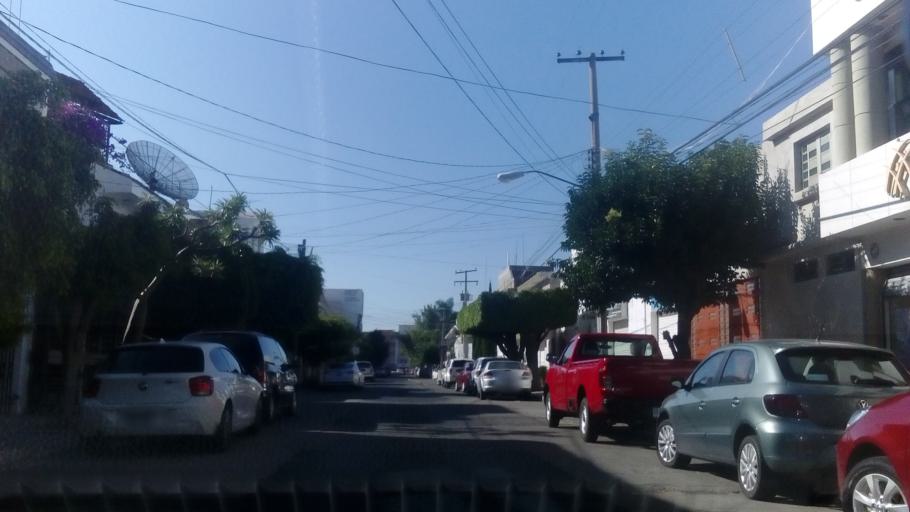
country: MX
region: Guanajuato
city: Leon
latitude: 21.1457
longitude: -101.6882
